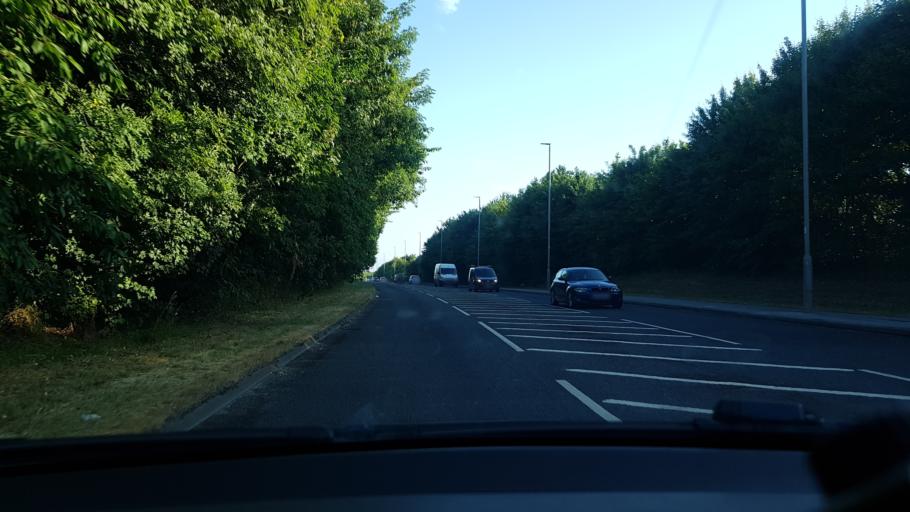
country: GB
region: England
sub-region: Nottinghamshire
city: Awsworth
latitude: 52.9835
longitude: -1.2907
